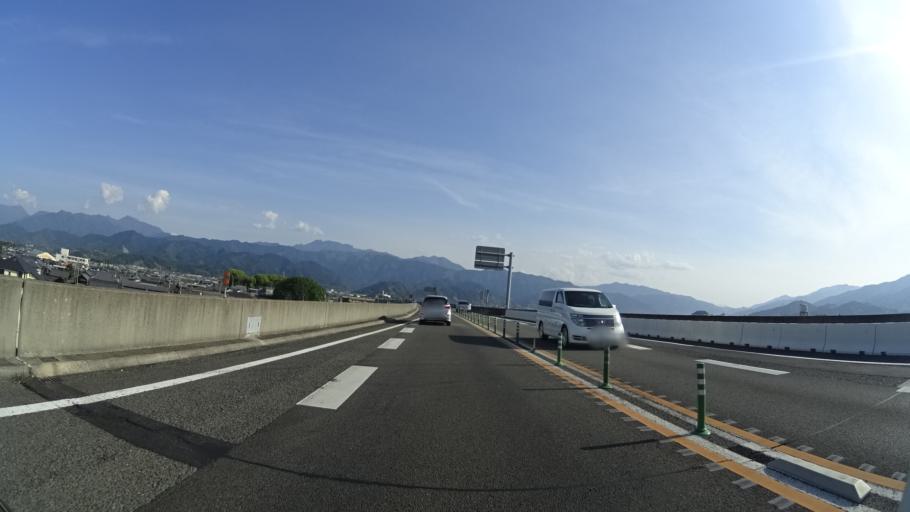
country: JP
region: Ehime
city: Saijo
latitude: 33.9146
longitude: 133.0727
